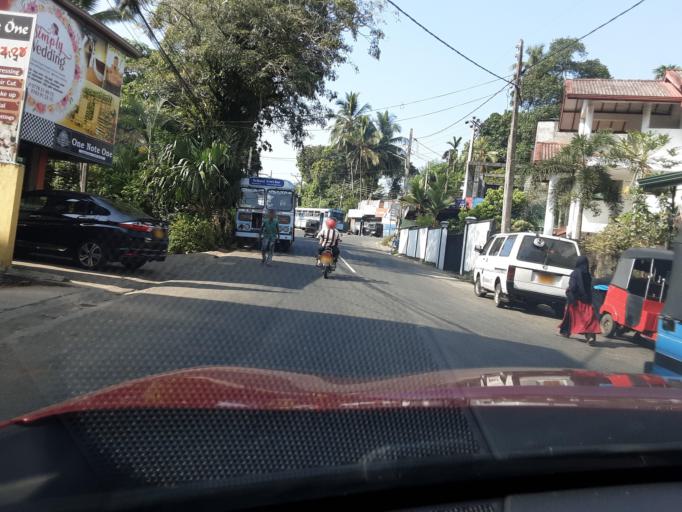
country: LK
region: Uva
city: Badulla
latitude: 6.9854
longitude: 81.0640
